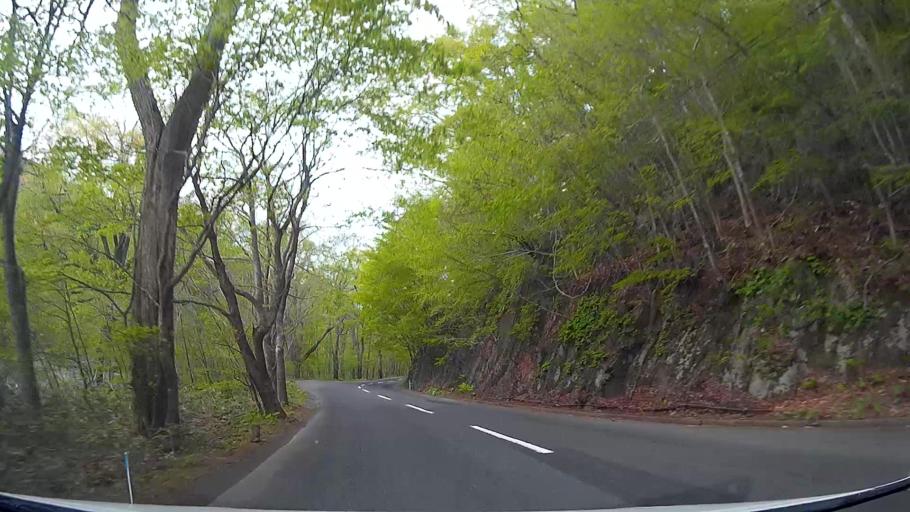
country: JP
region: Aomori
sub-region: Aomori Shi
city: Furudate
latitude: 40.5709
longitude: 140.9790
